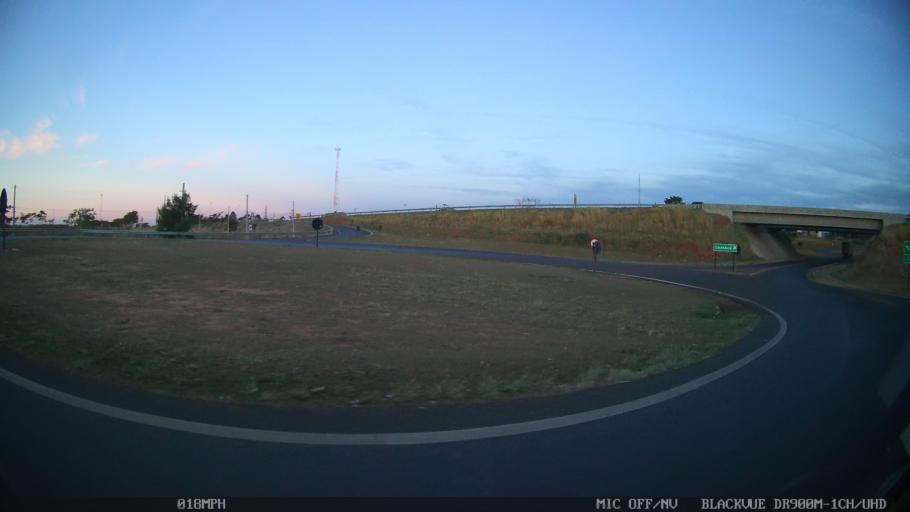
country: BR
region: Sao Paulo
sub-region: Catanduva
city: Catanduva
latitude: -21.1078
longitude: -48.9618
